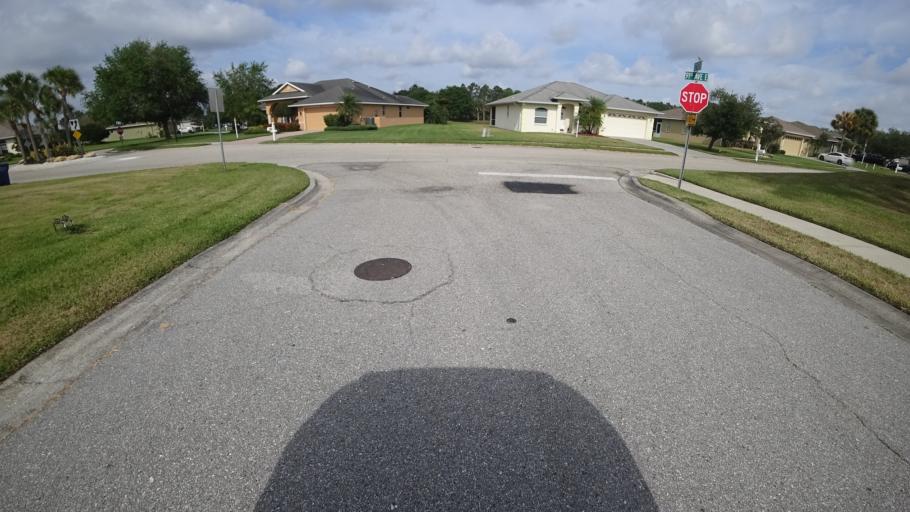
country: US
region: Florida
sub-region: Manatee County
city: Ellenton
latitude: 27.5706
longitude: -82.4716
